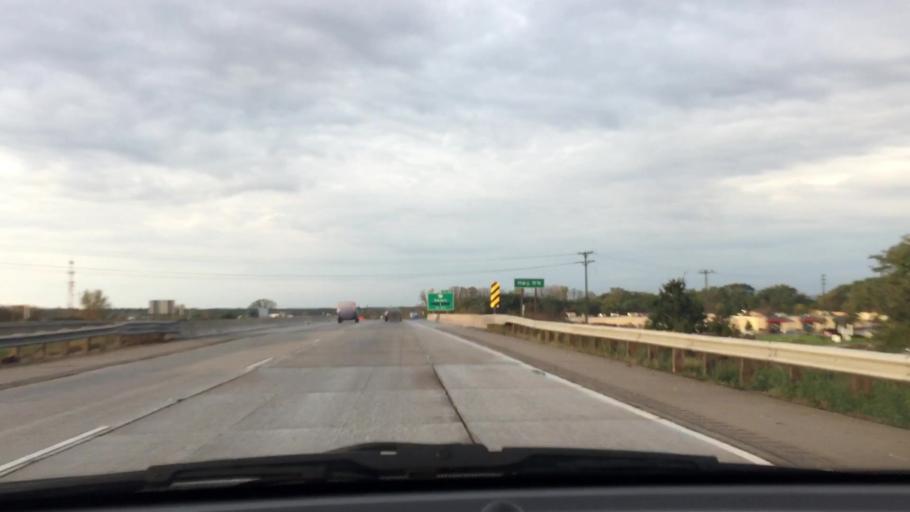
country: US
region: Wisconsin
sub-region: Walworth County
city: Elkhorn
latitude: 42.6708
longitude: -88.5260
